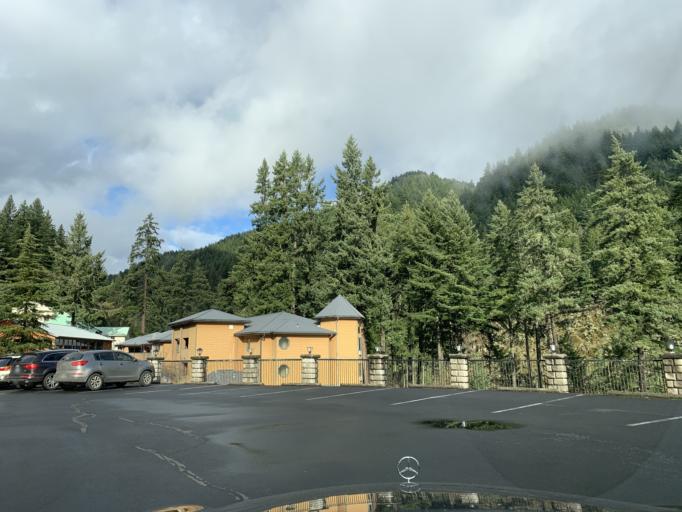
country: US
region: Washington
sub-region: Skamania County
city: Carson
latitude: 45.7280
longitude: -121.7969
